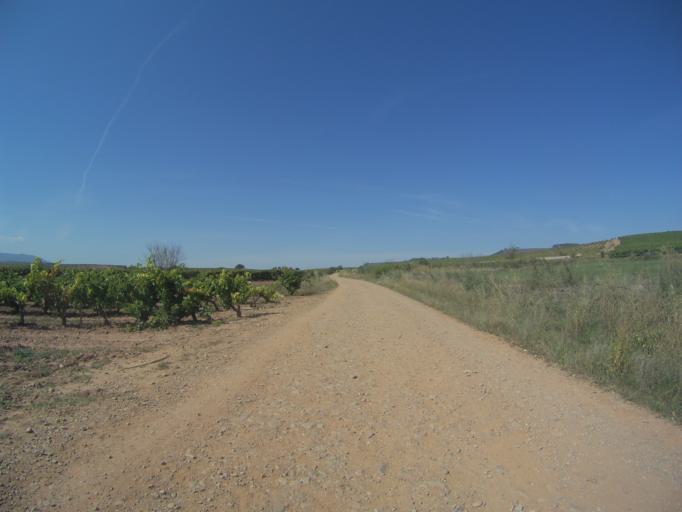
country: ES
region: La Rioja
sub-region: Provincia de La Rioja
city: Alesanco
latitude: 42.4288
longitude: -2.8155
